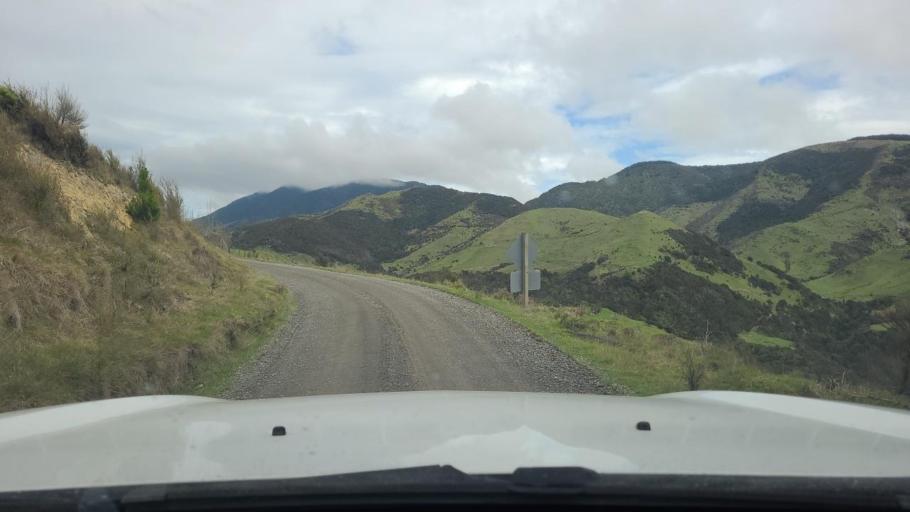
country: NZ
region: Wellington
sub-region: South Wairarapa District
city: Waipawa
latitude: -41.3589
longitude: 175.3920
